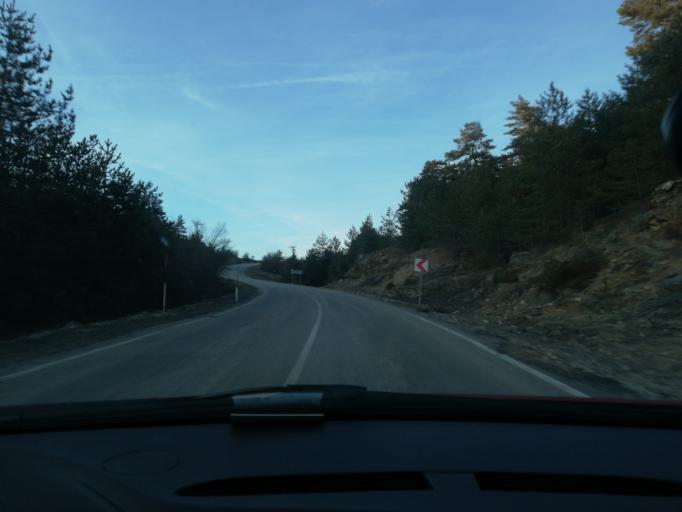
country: TR
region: Kastamonu
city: Agli
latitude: 41.7111
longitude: 33.6536
